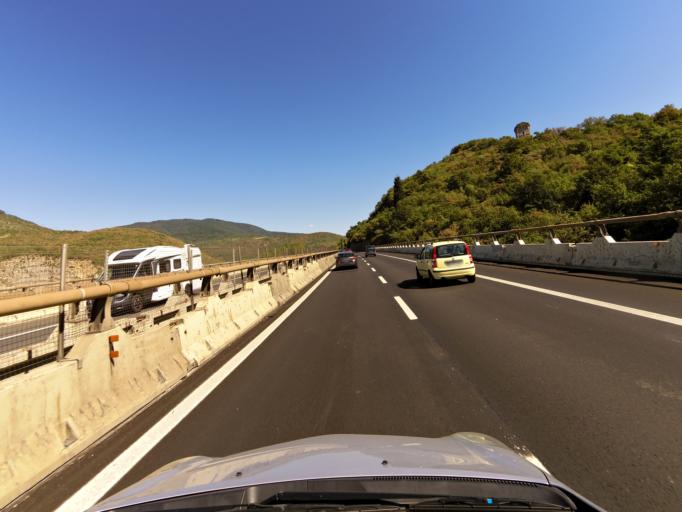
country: IT
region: Tuscany
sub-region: Province of Florence
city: Carraia
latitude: 43.9049
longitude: 11.1946
